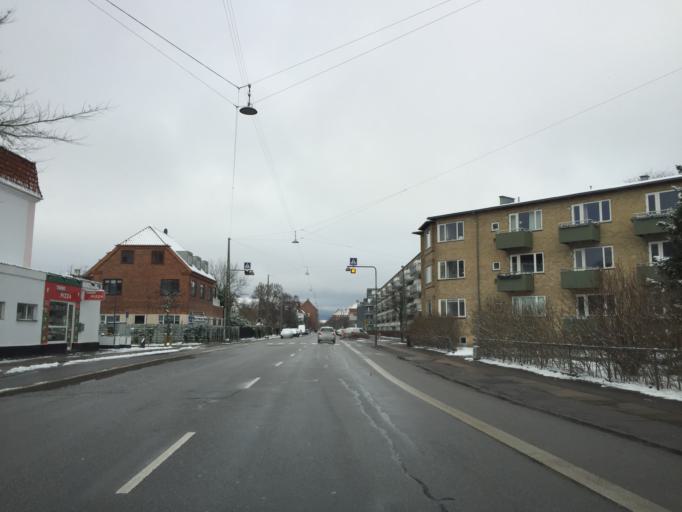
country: DK
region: Capital Region
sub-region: Kobenhavn
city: Christianshavn
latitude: 55.6581
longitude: 12.6200
